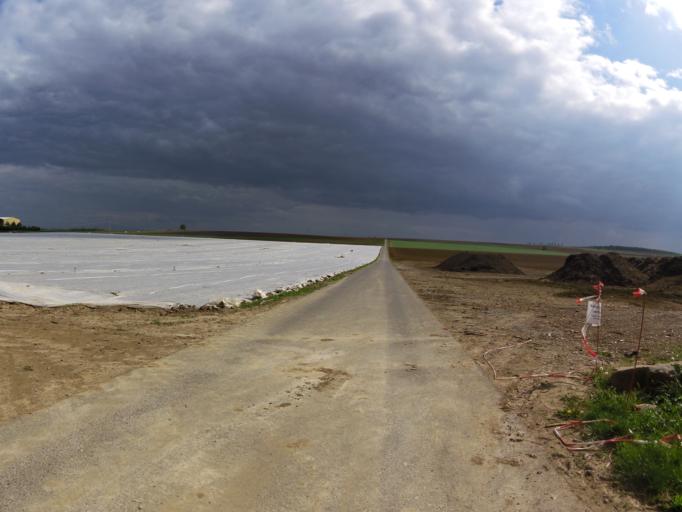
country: DE
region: Bavaria
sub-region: Regierungsbezirk Unterfranken
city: Oberpleichfeld
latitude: 49.8666
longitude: 10.0808
